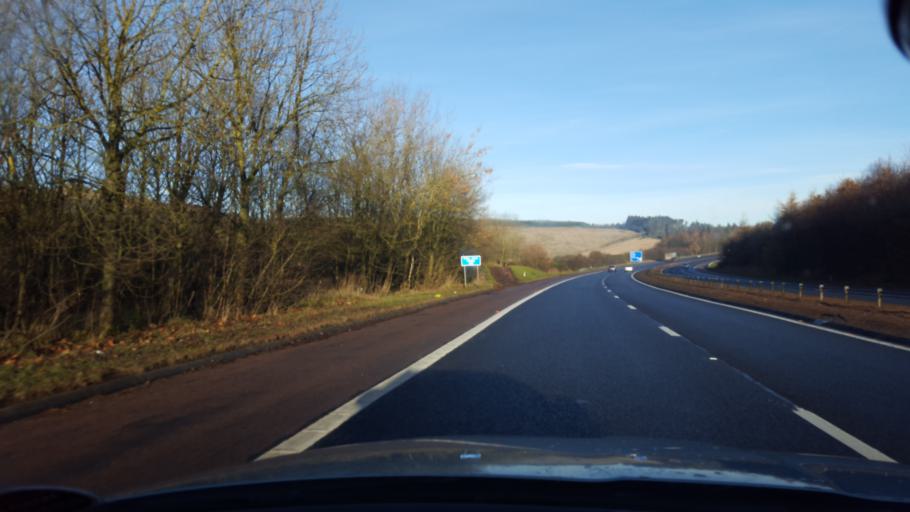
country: GB
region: Scotland
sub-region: Fife
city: Kelty
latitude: 56.1141
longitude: -3.3937
